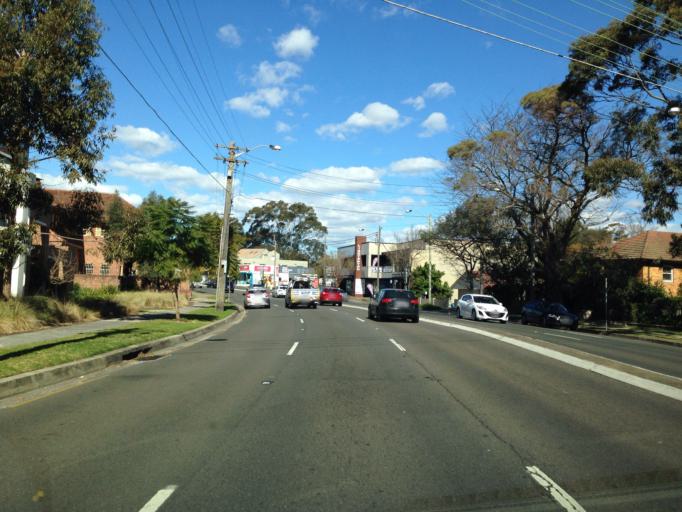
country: AU
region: New South Wales
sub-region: Ku-ring-gai
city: Killara
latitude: -33.7621
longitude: 151.1551
